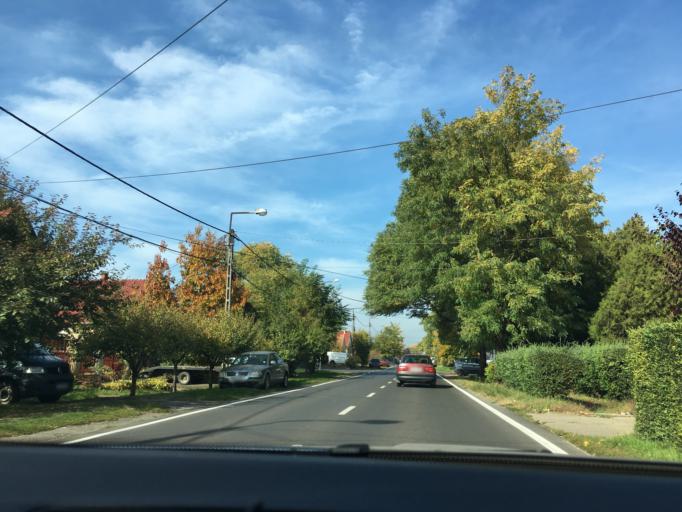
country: HU
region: Hajdu-Bihar
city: Debrecen
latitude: 47.5437
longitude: 21.6714
